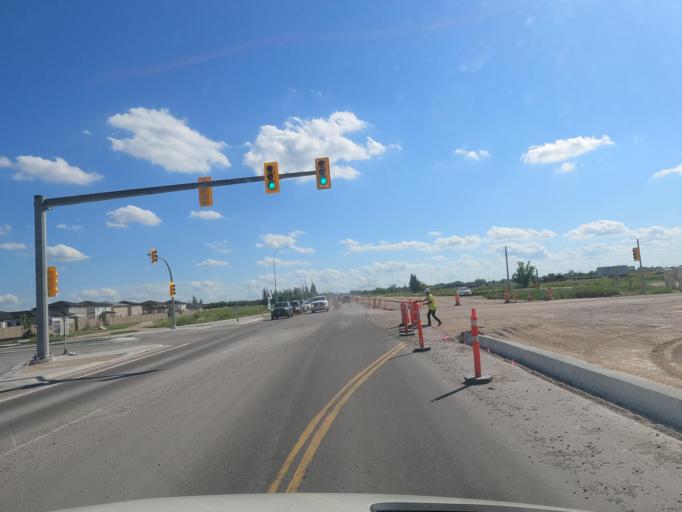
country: CA
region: Manitoba
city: Winnipeg
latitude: 49.9769
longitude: -97.0696
